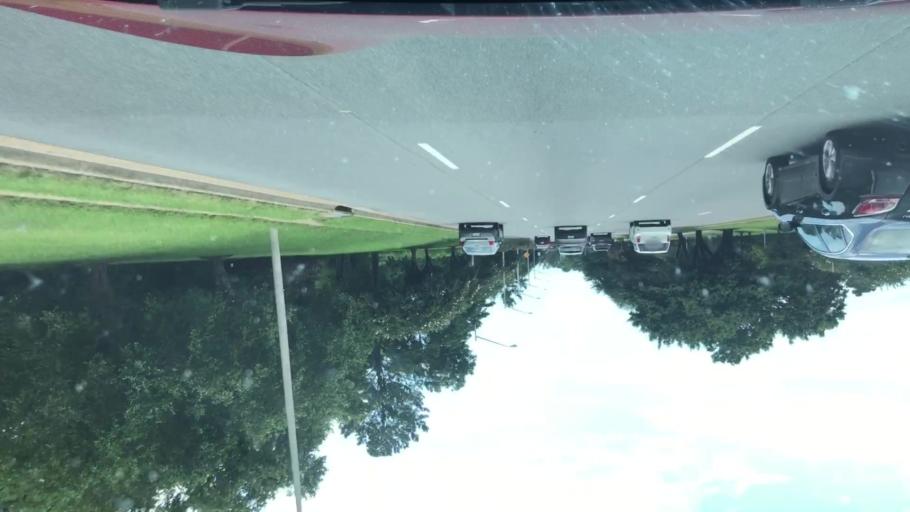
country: US
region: Virginia
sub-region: City of Chesapeake
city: Chesapeake
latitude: 36.8483
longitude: -76.1366
